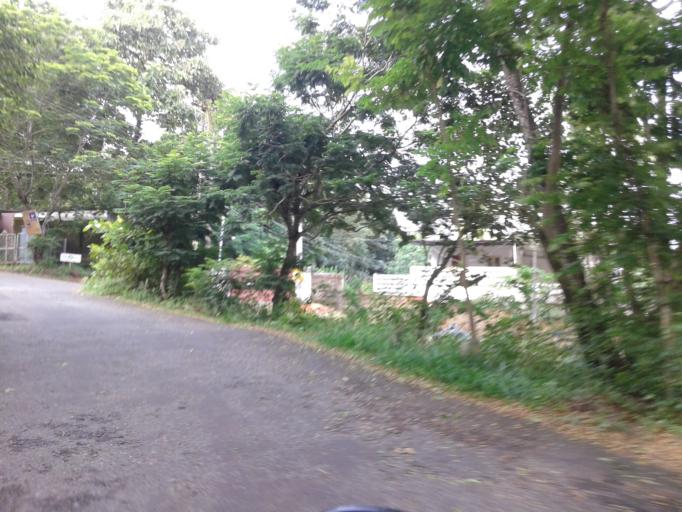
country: IN
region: Kerala
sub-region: Kozhikode
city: Kozhikode
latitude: 11.2950
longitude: 75.8050
